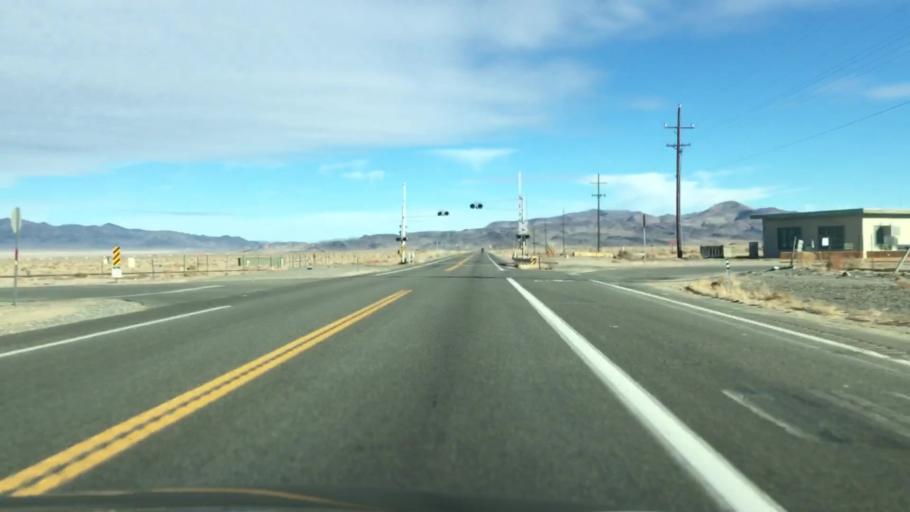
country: US
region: Nevada
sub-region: Mineral County
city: Hawthorne
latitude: 38.5245
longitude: -118.5989
